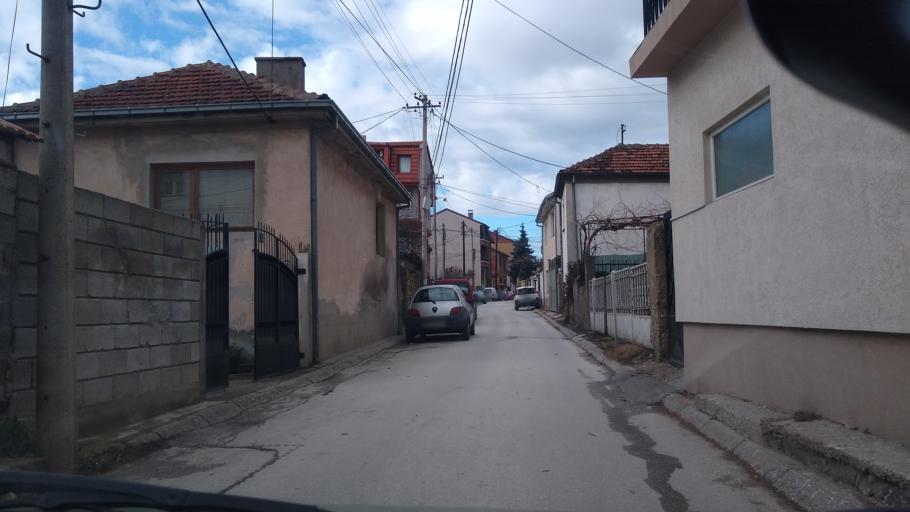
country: MK
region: Bitola
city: Bitola
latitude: 41.0286
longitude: 21.3254
